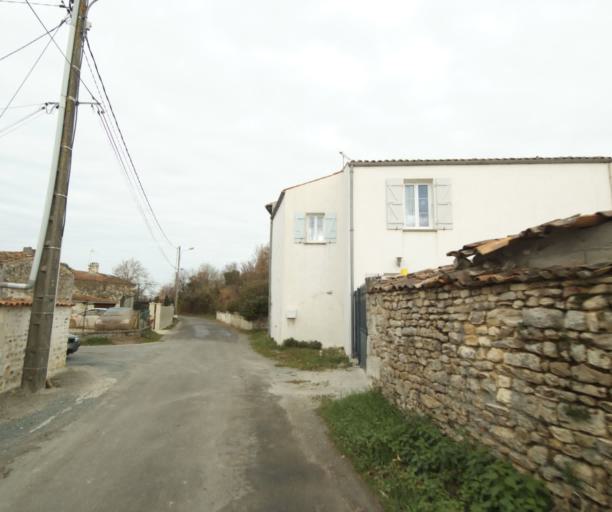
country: FR
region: Poitou-Charentes
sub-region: Departement de la Charente-Maritime
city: Corme-Royal
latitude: 45.7348
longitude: -0.7861
